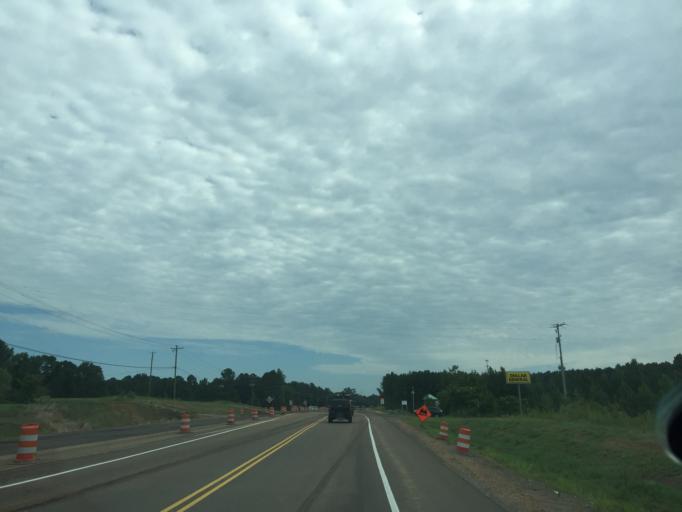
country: US
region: Mississippi
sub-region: Rankin County
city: Brandon
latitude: 32.2972
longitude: -89.9960
